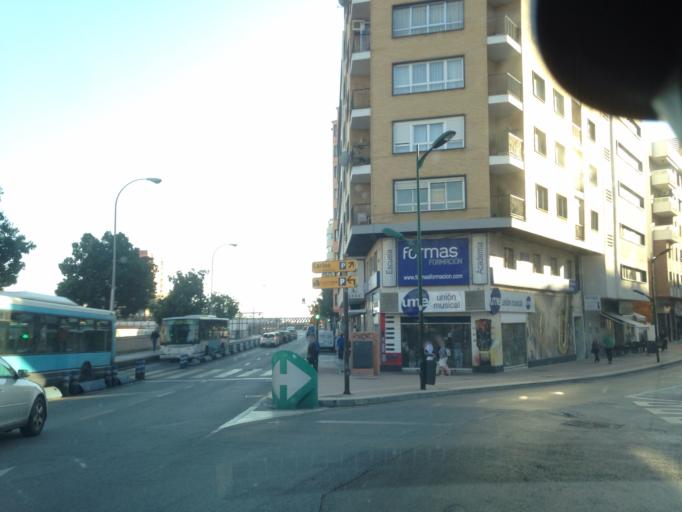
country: ES
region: Andalusia
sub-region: Provincia de Malaga
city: Malaga
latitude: 36.7156
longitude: -4.4264
